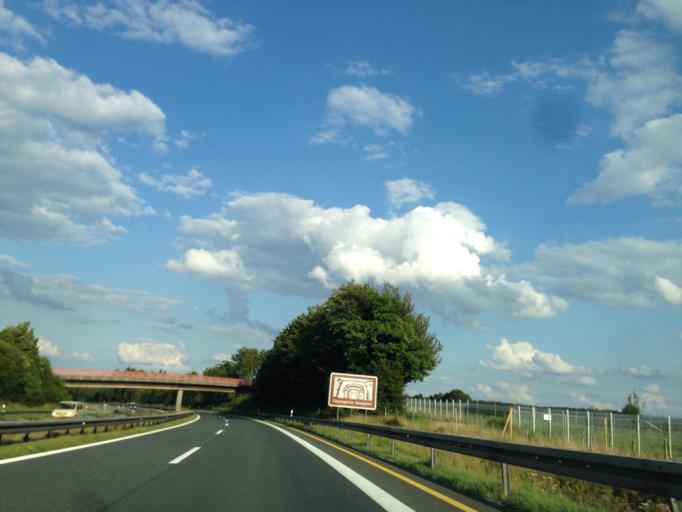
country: DE
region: Bavaria
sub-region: Upper Franconia
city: Wonsees
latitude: 50.0052
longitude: 11.2882
